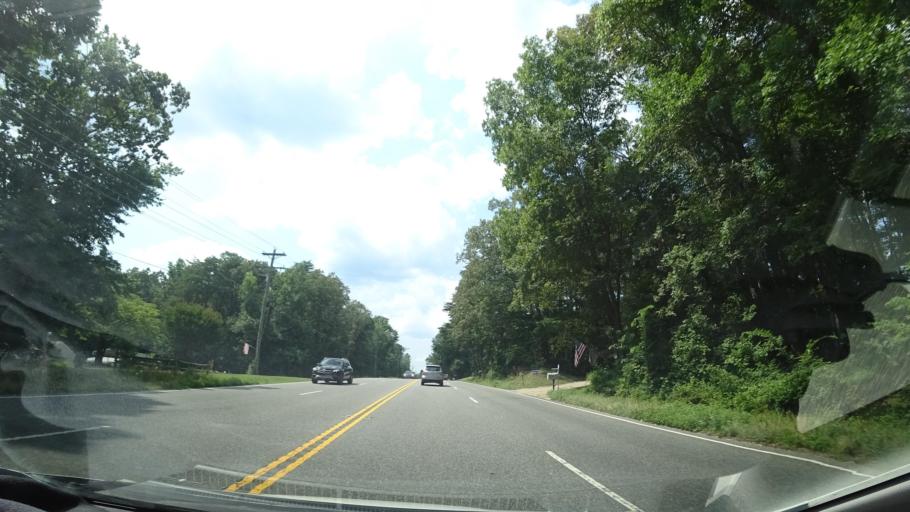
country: US
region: Virginia
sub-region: Hanover County
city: Ashland
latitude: 37.8991
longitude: -77.4689
